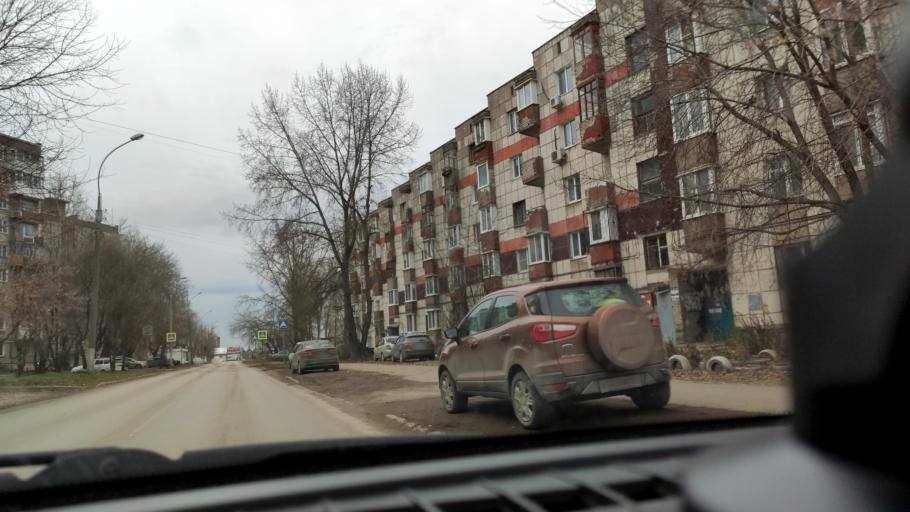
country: RU
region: Perm
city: Kondratovo
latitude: 57.9627
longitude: 56.1692
